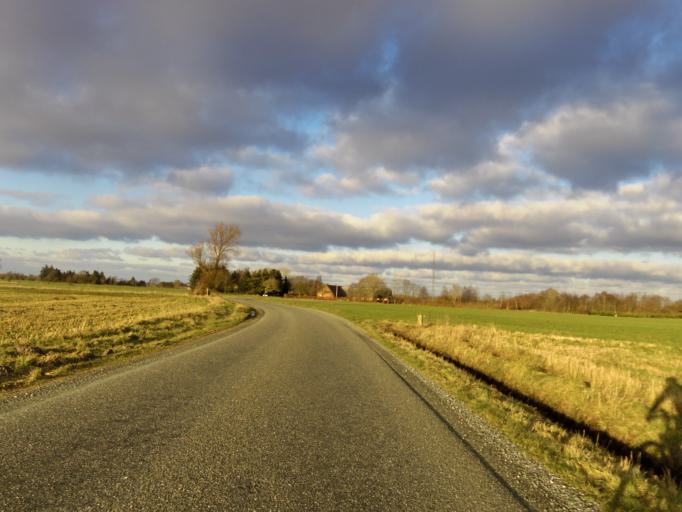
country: DK
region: South Denmark
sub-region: Esbjerg Kommune
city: Ribe
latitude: 55.2887
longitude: 8.8470
